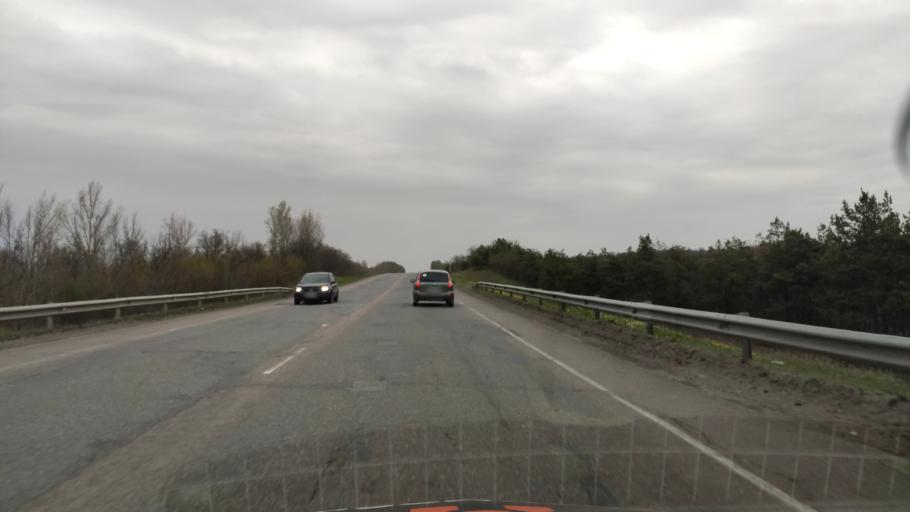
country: RU
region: Kursk
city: Gorshechnoye
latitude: 51.4444
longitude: 37.9106
